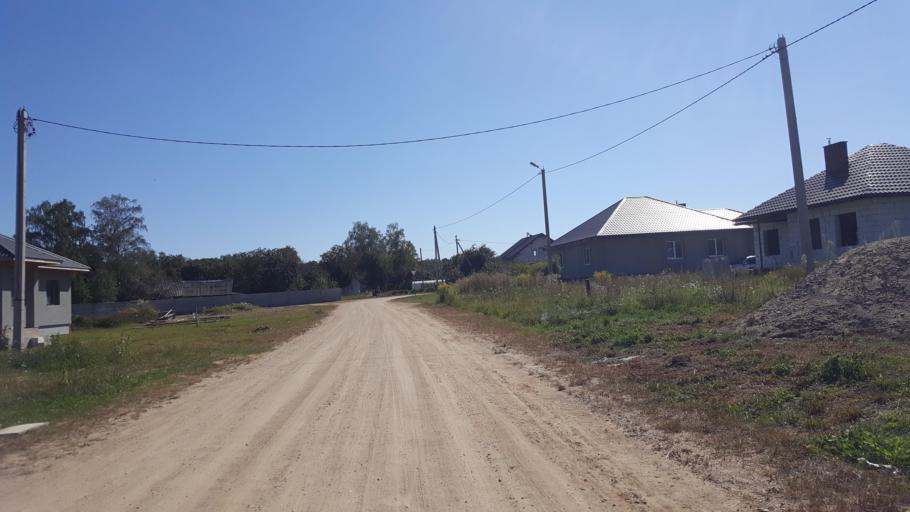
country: BY
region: Brest
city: Vysokaye
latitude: 52.2523
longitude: 23.4986
